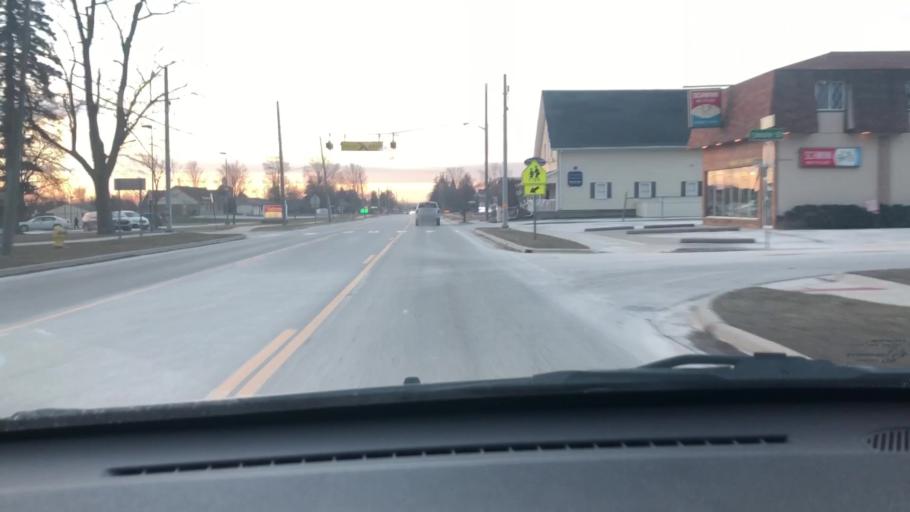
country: US
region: Michigan
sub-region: Macomb County
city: Shelby
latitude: 42.7234
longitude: -83.0358
